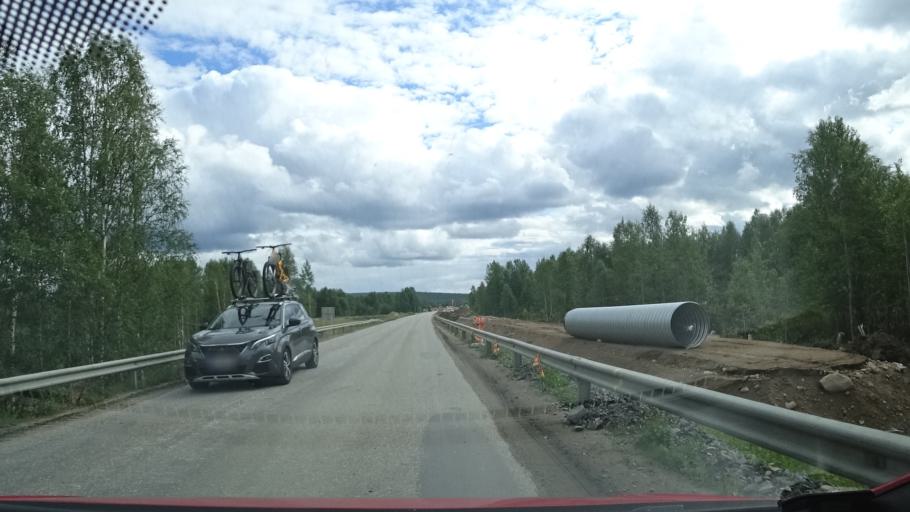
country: FI
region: Lapland
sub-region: Rovaniemi
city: Rovaniemi
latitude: 66.5270
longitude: 25.7419
